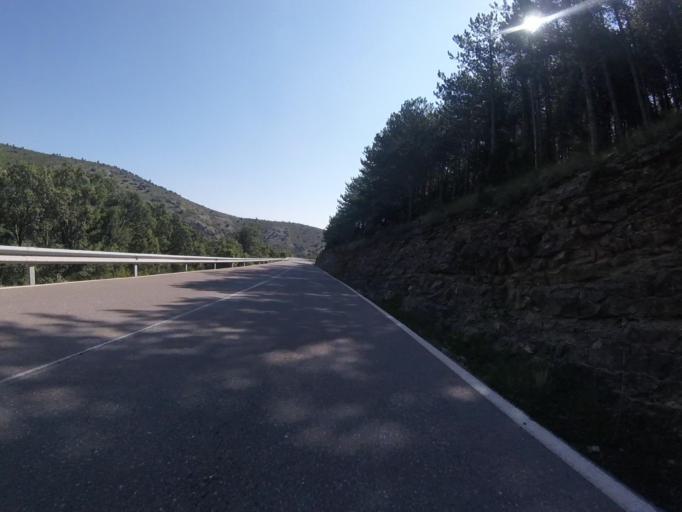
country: ES
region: Valencia
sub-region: Provincia de Castello
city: Benafigos
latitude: 40.2678
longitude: -0.2391
